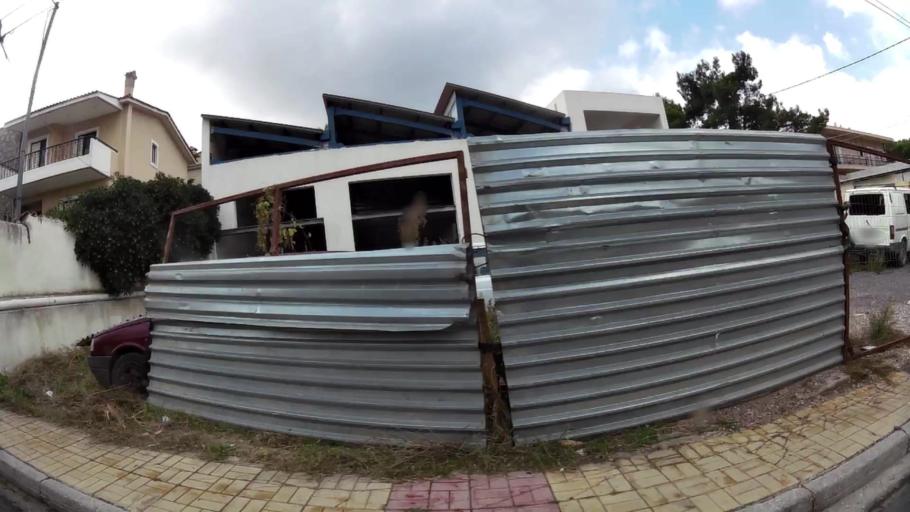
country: GR
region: Attica
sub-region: Nomarchia Athinas
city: Melissia
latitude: 38.0611
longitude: 23.8347
